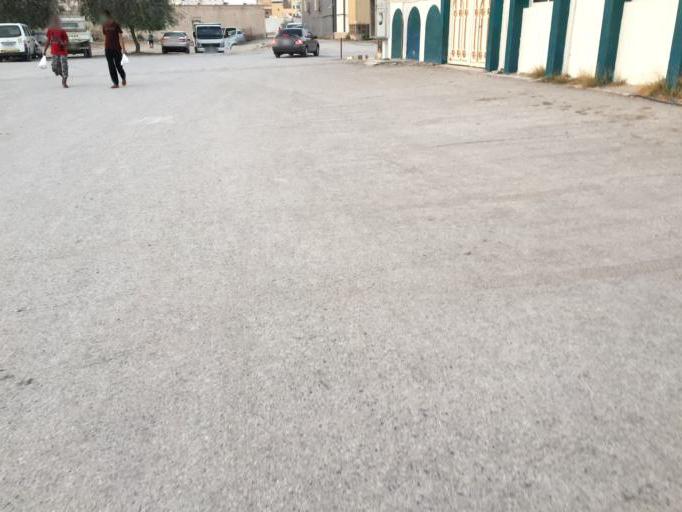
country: AE
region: Ra's al Khaymah
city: Ras al-Khaimah
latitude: 25.7931
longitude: 55.9736
